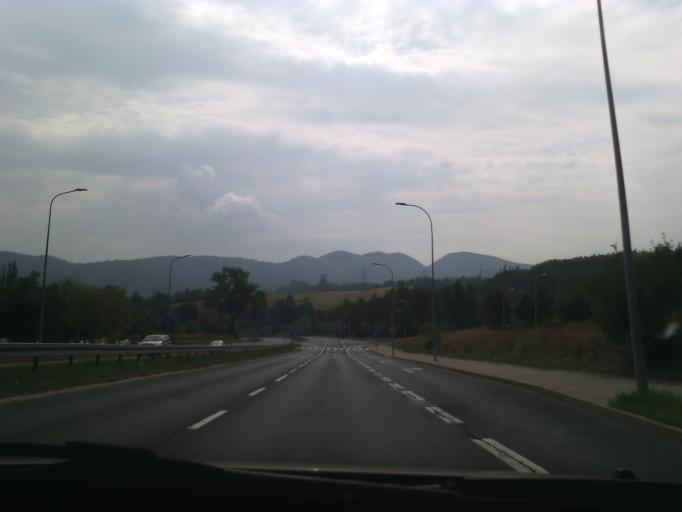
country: PL
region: Lower Silesian Voivodeship
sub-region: Powiat walbrzyski
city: Walbrzych
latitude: 50.7592
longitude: 16.2756
